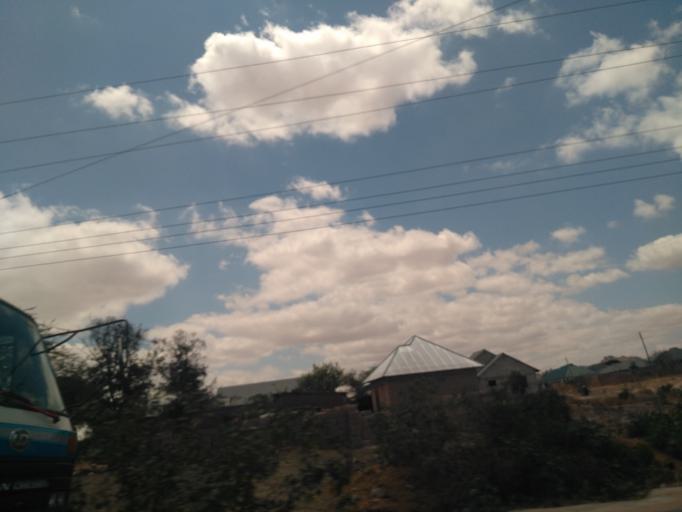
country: TZ
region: Dodoma
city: Kisasa
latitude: -6.1788
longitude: 35.7992
